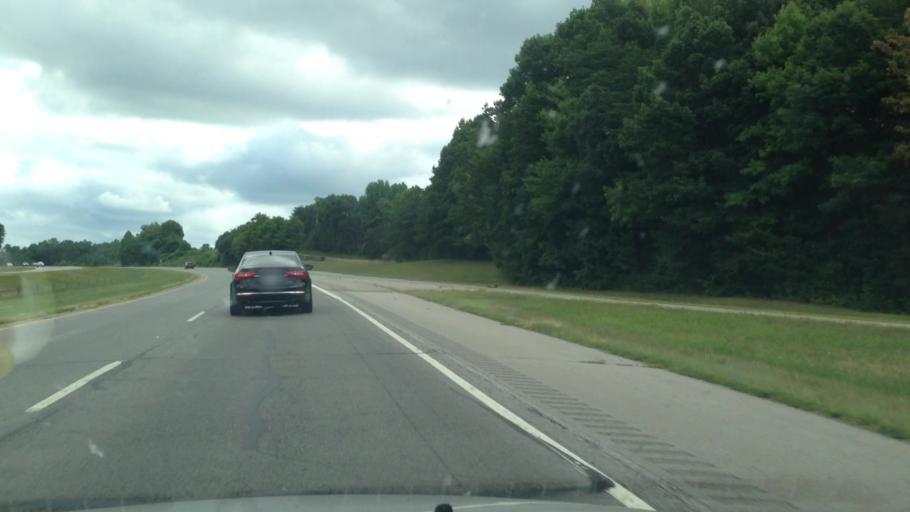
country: US
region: Virginia
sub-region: City of Danville
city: Danville
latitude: 36.4888
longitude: -79.4882
